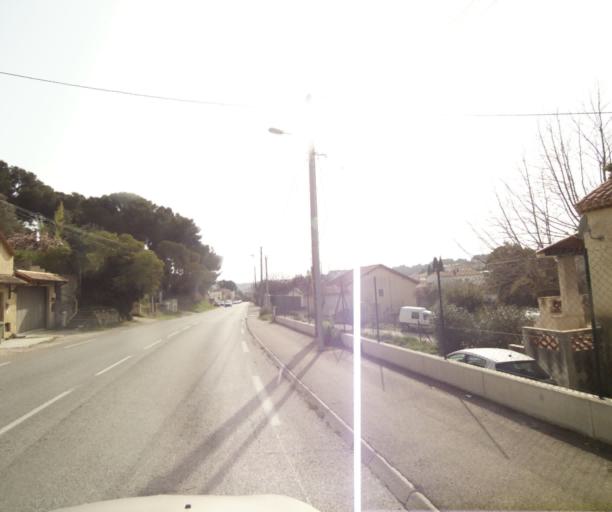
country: FR
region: Provence-Alpes-Cote d'Azur
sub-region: Departement des Bouches-du-Rhone
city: Septemes-les-Vallons
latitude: 43.3935
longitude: 5.3441
